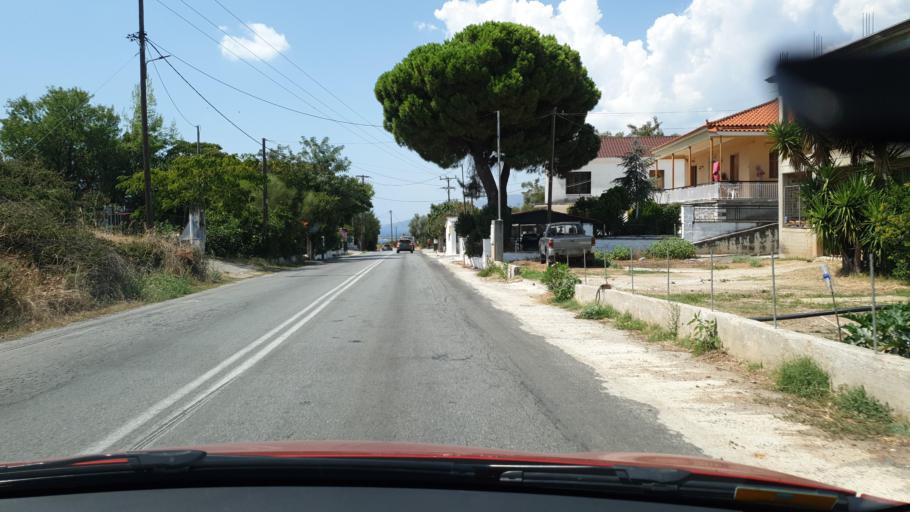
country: GR
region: Central Greece
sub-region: Nomos Evvoias
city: Aliveri
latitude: 38.3924
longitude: 24.0849
